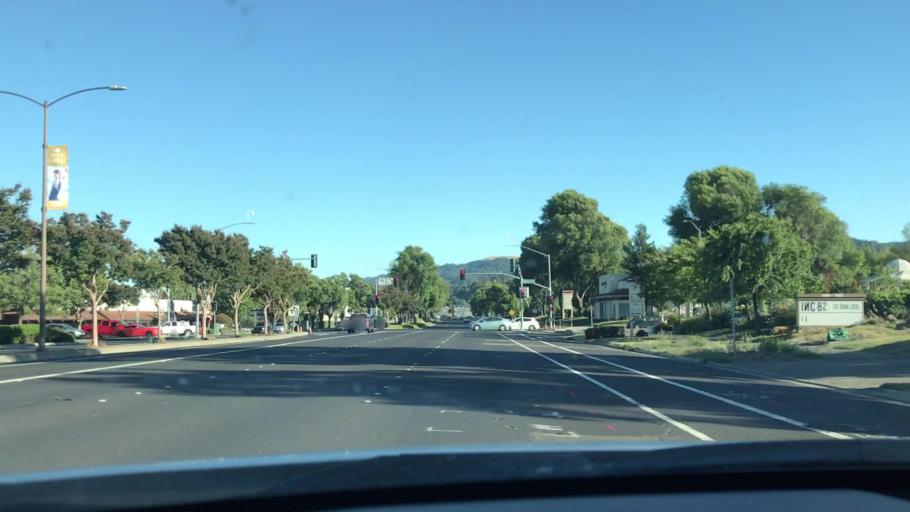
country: US
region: California
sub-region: Alameda County
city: Dublin
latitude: 37.7064
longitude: -121.9370
